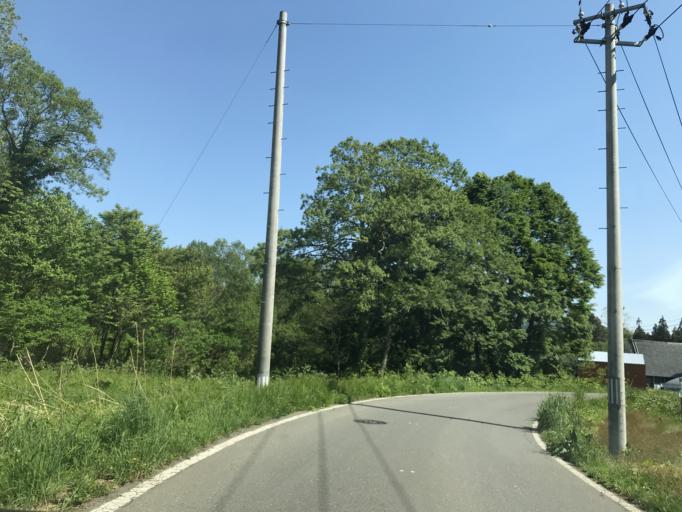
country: JP
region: Iwate
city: Shizukuishi
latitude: 39.5596
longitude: 140.8412
